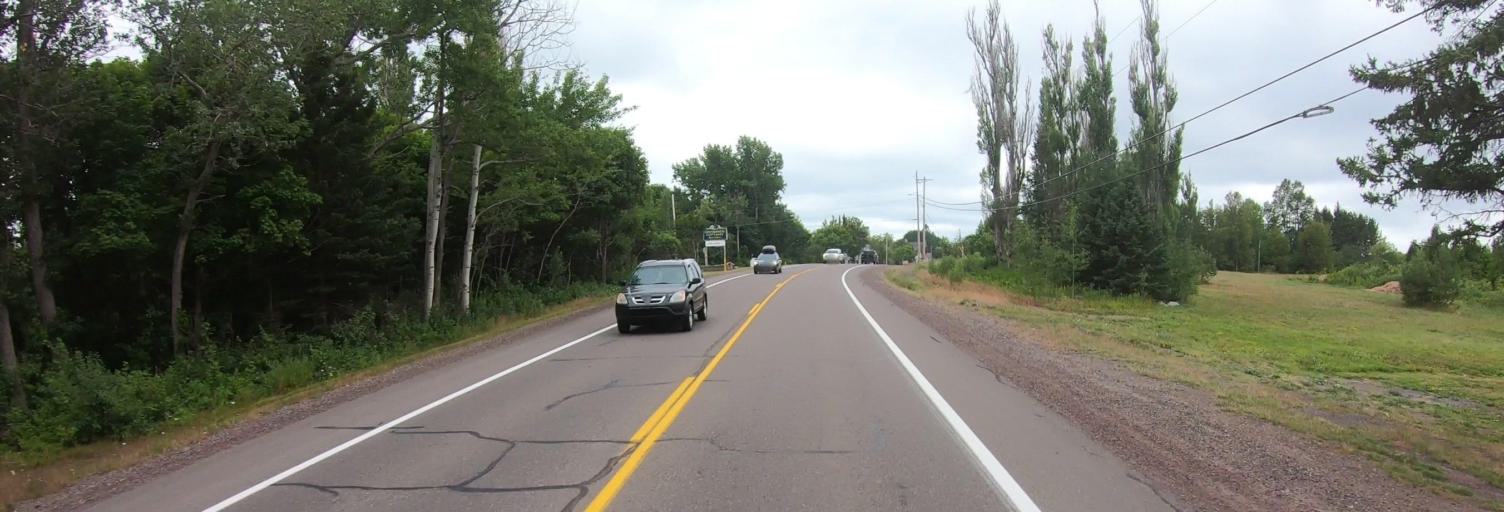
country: US
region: Michigan
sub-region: Houghton County
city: Laurium
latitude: 47.2610
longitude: -88.4265
